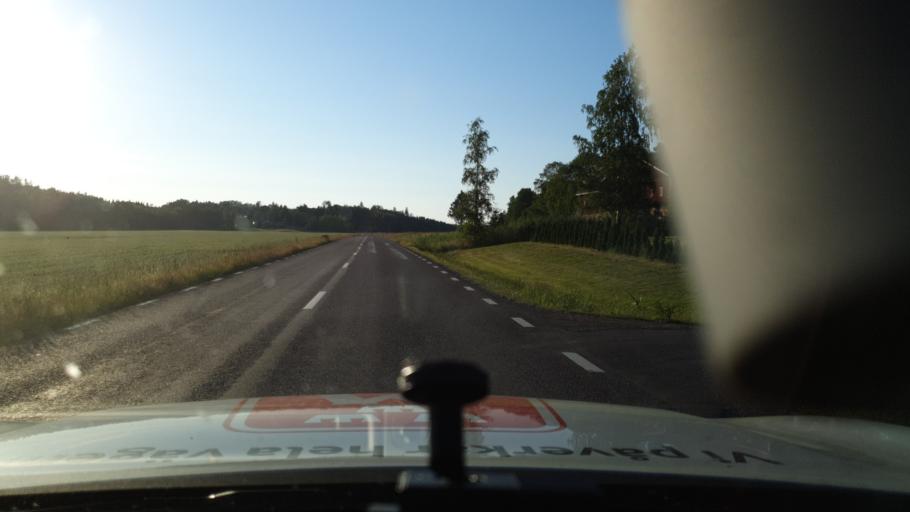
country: SE
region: Vaermland
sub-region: Kils Kommun
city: Kil
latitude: 59.5463
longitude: 13.2940
